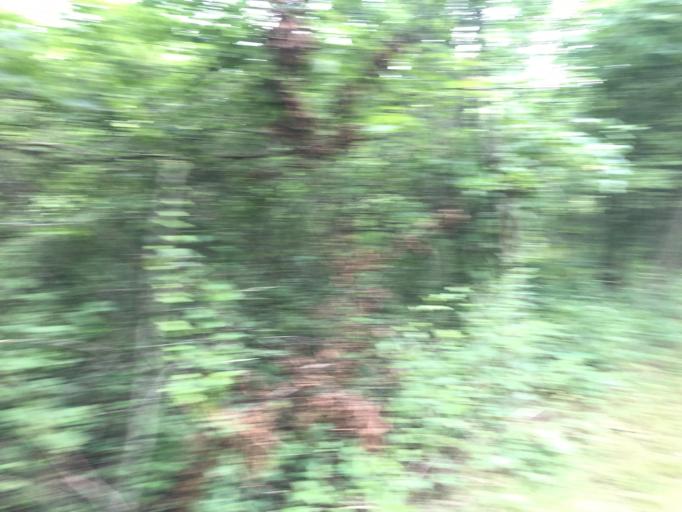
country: US
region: Pennsylvania
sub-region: Montgomery County
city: Blue Bell
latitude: 40.1589
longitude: -75.2549
